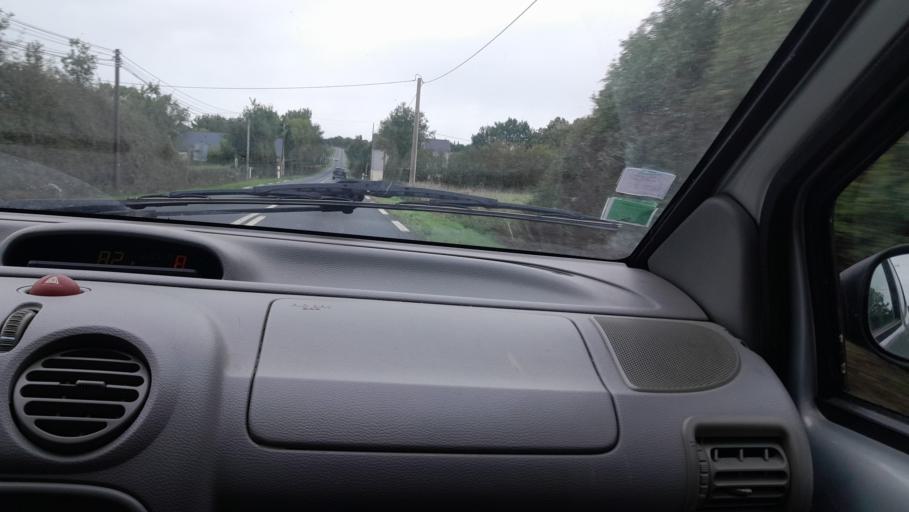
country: FR
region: Pays de la Loire
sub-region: Departement de la Loire-Atlantique
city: Saint-Mars-la-Jaille
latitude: 47.4893
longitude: -1.1737
